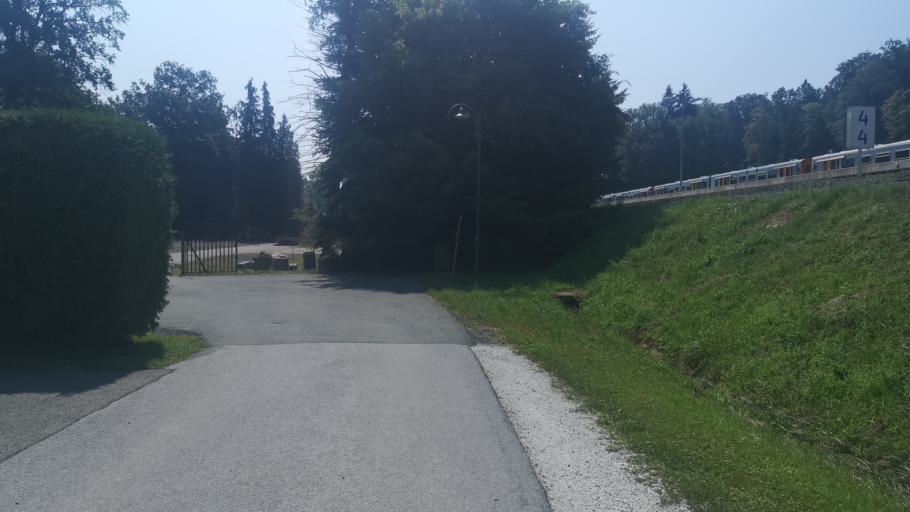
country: AT
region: Styria
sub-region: Politischer Bezirk Deutschlandsberg
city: Lannach
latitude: 46.9408
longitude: 15.3349
